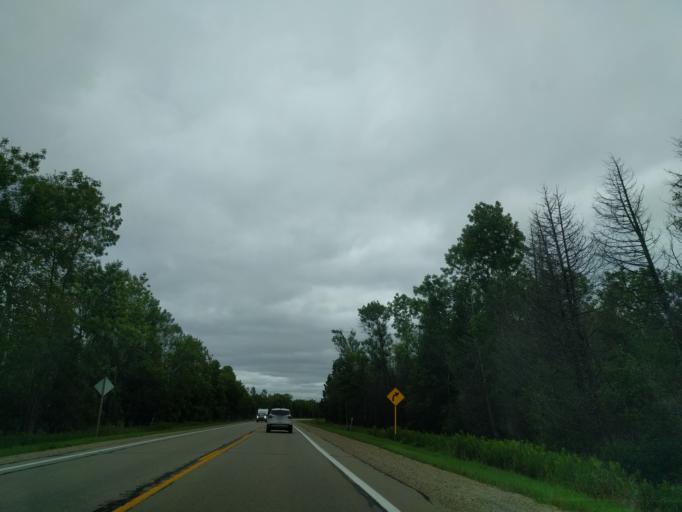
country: US
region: Michigan
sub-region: Menominee County
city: Menominee
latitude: 45.4230
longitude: -87.3489
